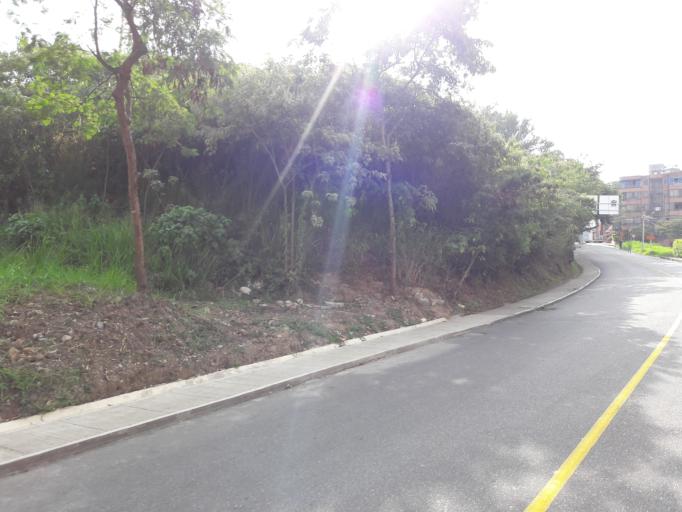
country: CO
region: Tolima
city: Ibague
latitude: 4.4365
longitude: -75.2064
